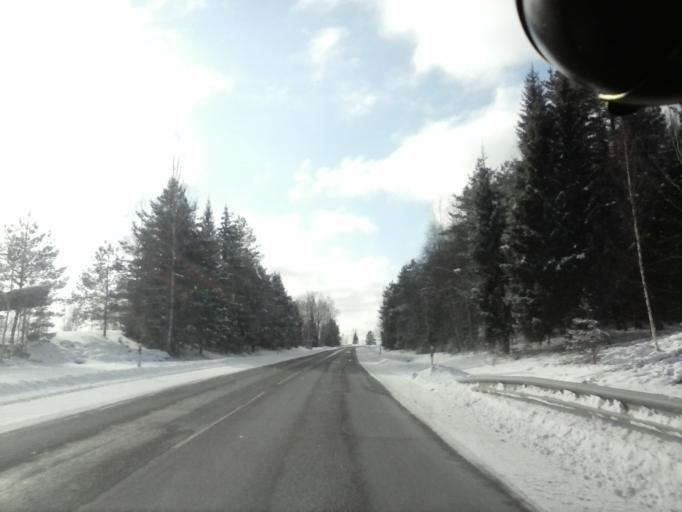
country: EE
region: Paernumaa
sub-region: Saarde vald
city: Kilingi-Nomme
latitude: 58.1825
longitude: 25.0518
